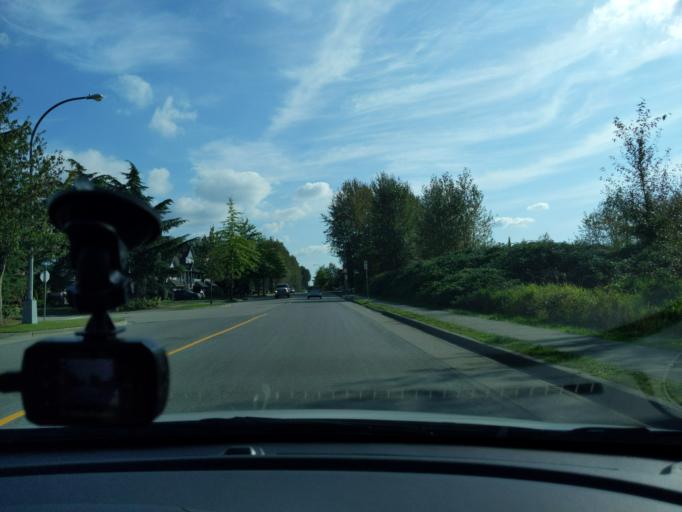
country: CA
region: British Columbia
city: Pitt Meadows
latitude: 49.2073
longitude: -122.6784
